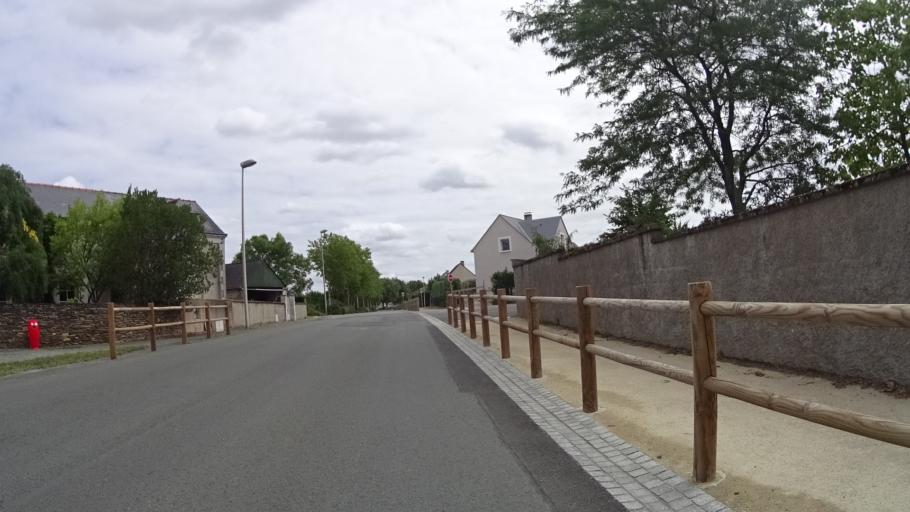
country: FR
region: Pays de la Loire
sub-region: Departement de Maine-et-Loire
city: Sainte-Gemmes-sur-Loire
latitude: 47.4213
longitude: -0.5688
